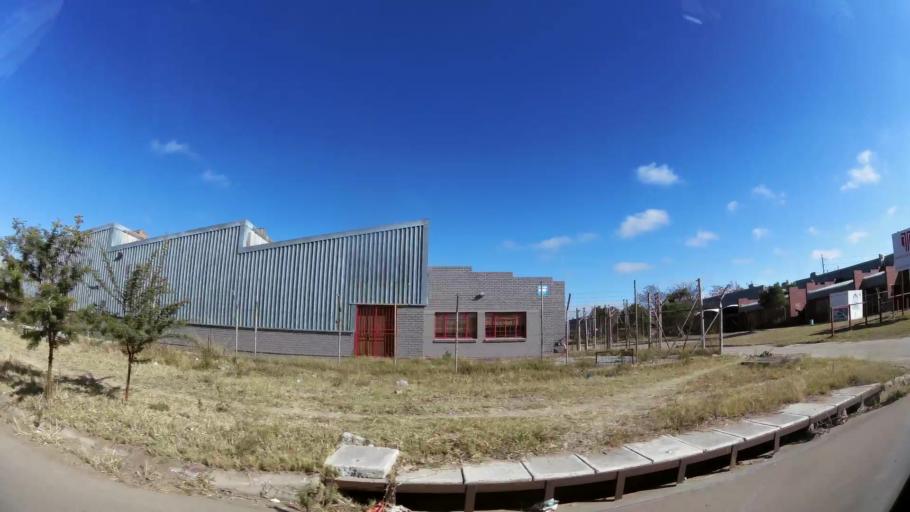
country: ZA
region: Limpopo
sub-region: Capricorn District Municipality
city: Polokwane
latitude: -23.8422
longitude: 29.4010
